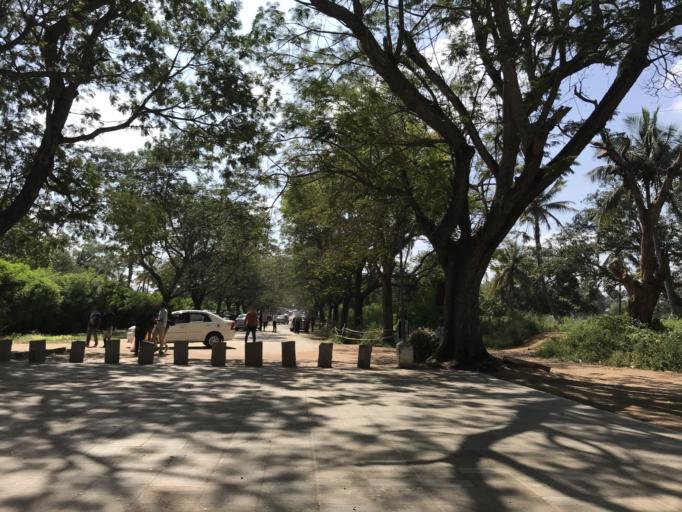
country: IN
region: Karnataka
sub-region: Mandya
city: Shrirangapattana
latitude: 12.4179
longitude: 76.6965
